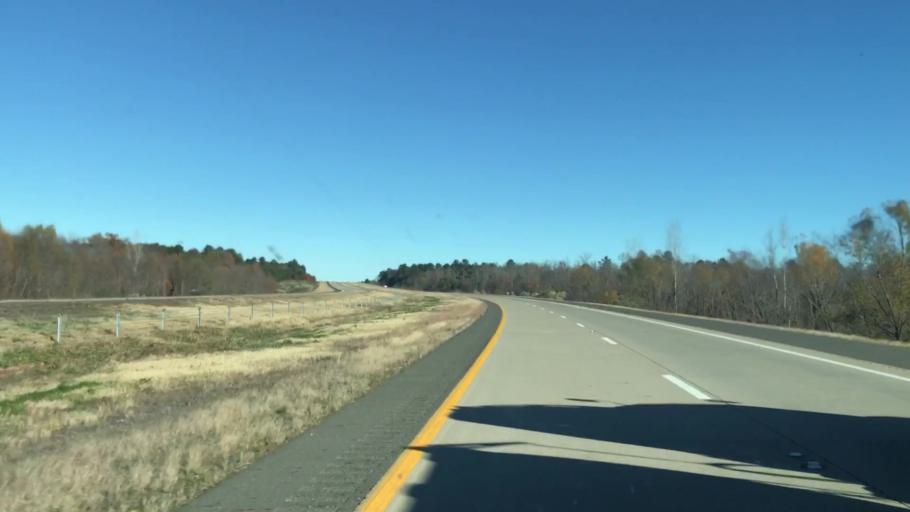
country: US
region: Texas
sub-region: Cass County
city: Queen City
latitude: 33.1696
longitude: -93.8780
